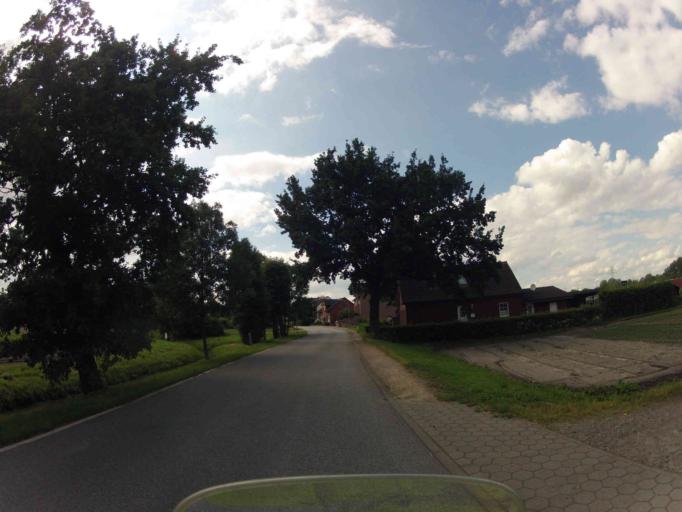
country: DE
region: Hamburg
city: Rothenburgsort
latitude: 53.5137
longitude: 10.0796
